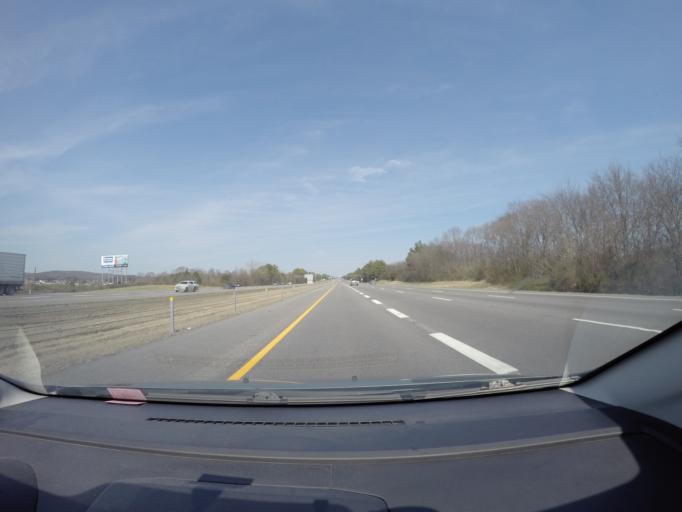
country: US
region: Tennessee
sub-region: Rutherford County
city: Smyrna
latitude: 35.8925
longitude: -86.4848
